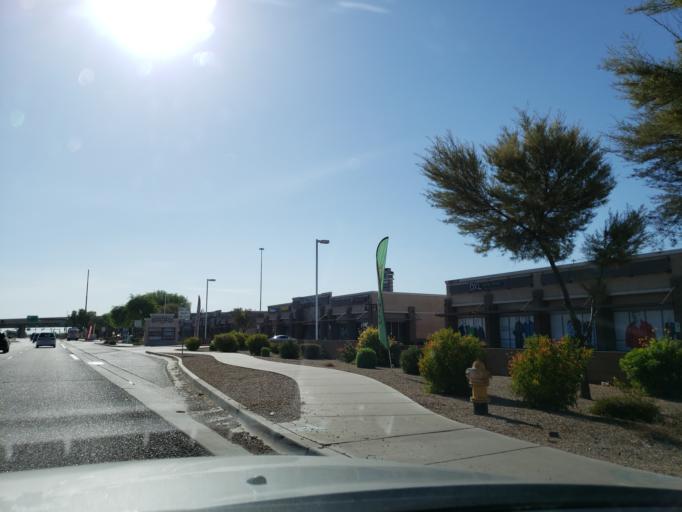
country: US
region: Arizona
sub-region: Maricopa County
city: Tolleson
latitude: 33.4647
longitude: -112.2722
